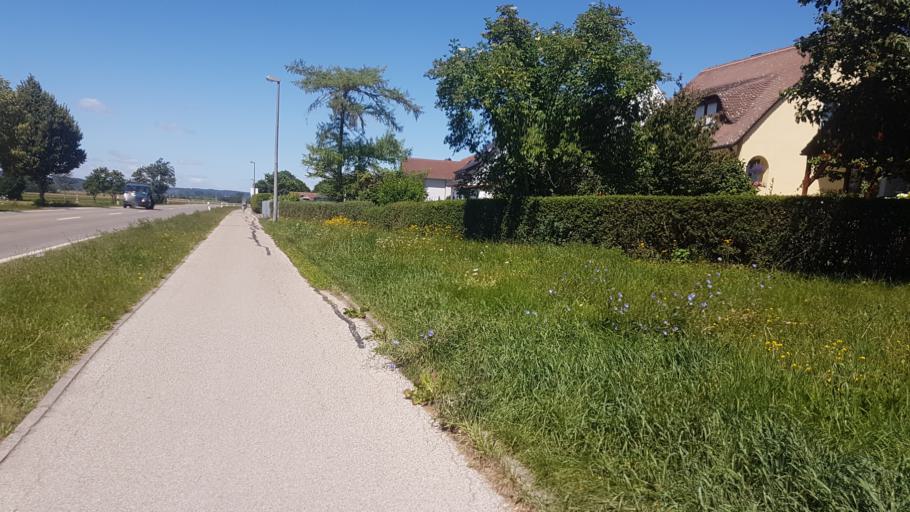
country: DE
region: Bavaria
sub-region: Regierungsbezirk Mittelfranken
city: Herrieden
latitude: 49.2352
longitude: 10.4898
